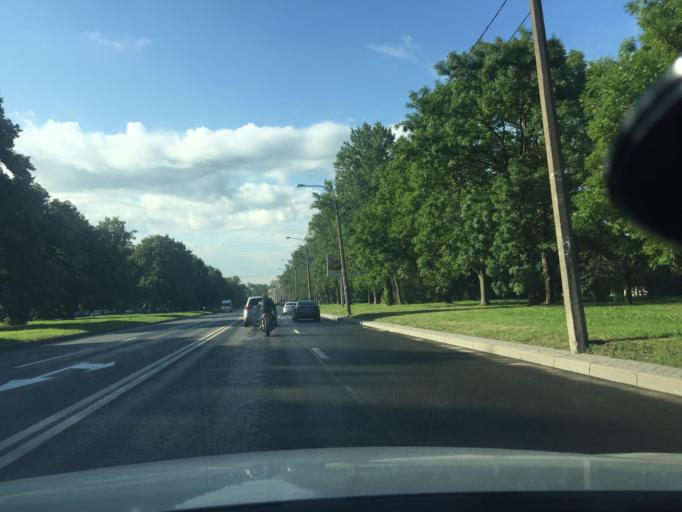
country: RU
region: St.-Petersburg
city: Kupchino
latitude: 59.8436
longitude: 30.3381
